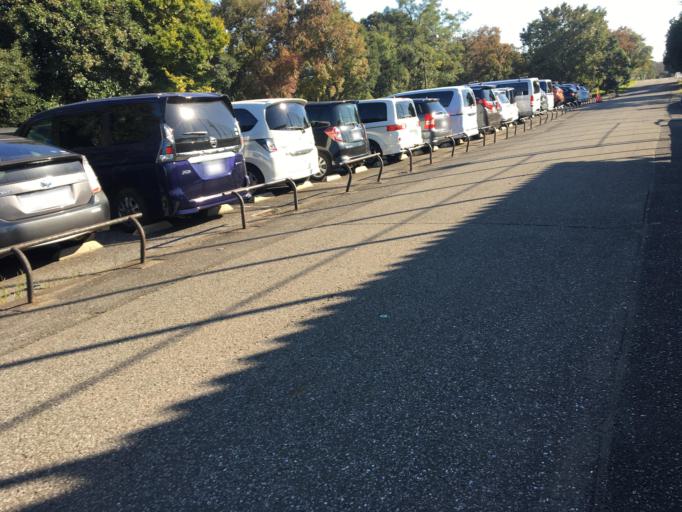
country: JP
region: Tokyo
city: Urayasu
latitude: 35.6514
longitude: 139.8240
